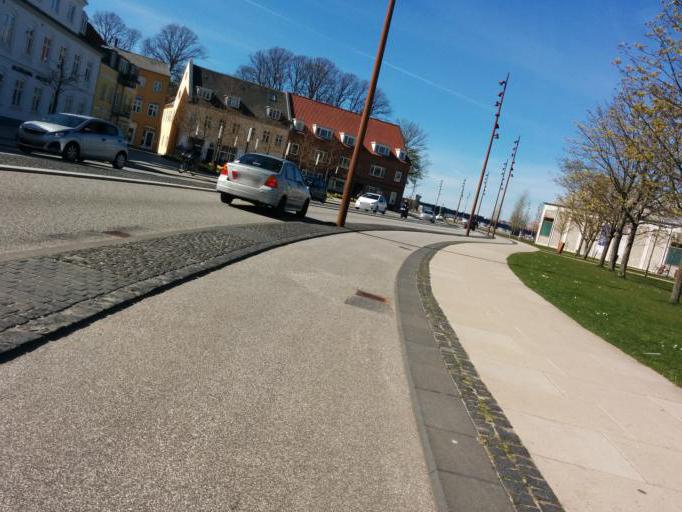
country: DK
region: North Denmark
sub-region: Alborg Kommune
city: Aalborg
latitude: 57.0485
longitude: 9.9263
